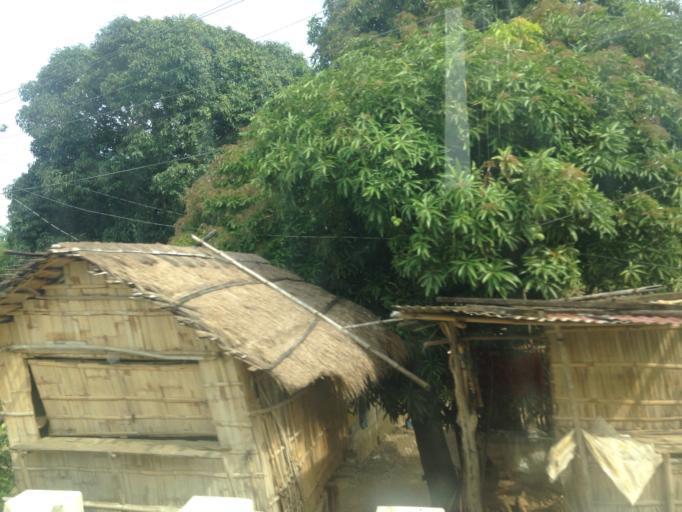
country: PH
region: Mimaropa
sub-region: Province of Mindoro Oriental
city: Bulalacao
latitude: 12.3838
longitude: 121.3510
